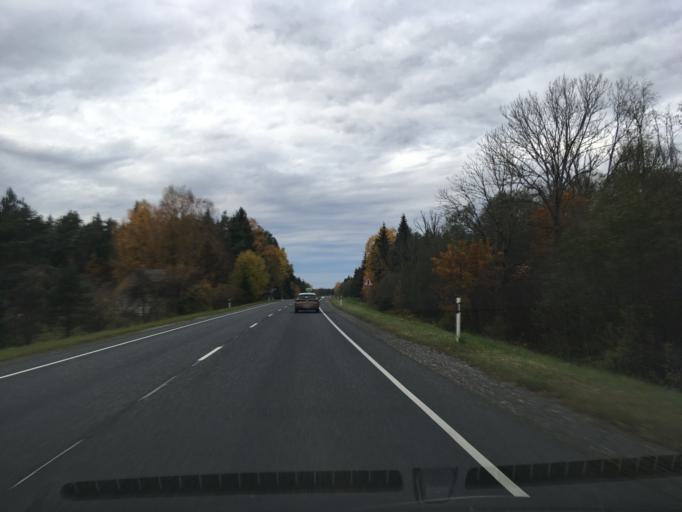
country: EE
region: Harju
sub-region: Nissi vald
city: Turba
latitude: 58.9324
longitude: 24.0990
